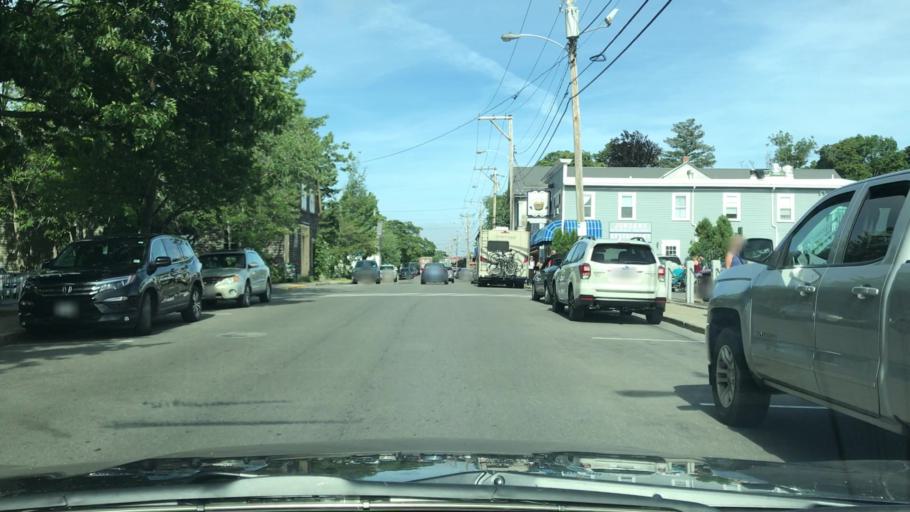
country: US
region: Maine
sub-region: Hancock County
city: Bar Harbor
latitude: 44.3889
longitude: -68.2108
